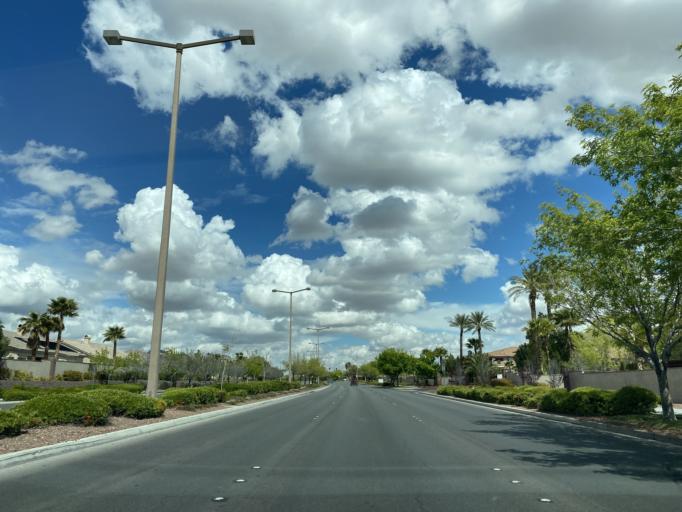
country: US
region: Nevada
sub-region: Clark County
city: Summerlin South
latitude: 36.1305
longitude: -115.3246
